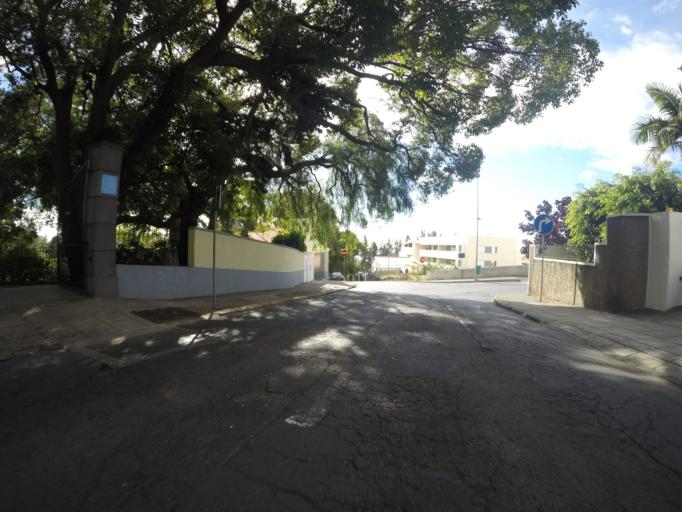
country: PT
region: Madeira
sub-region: Funchal
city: Funchal
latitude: 32.6418
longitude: -16.9276
